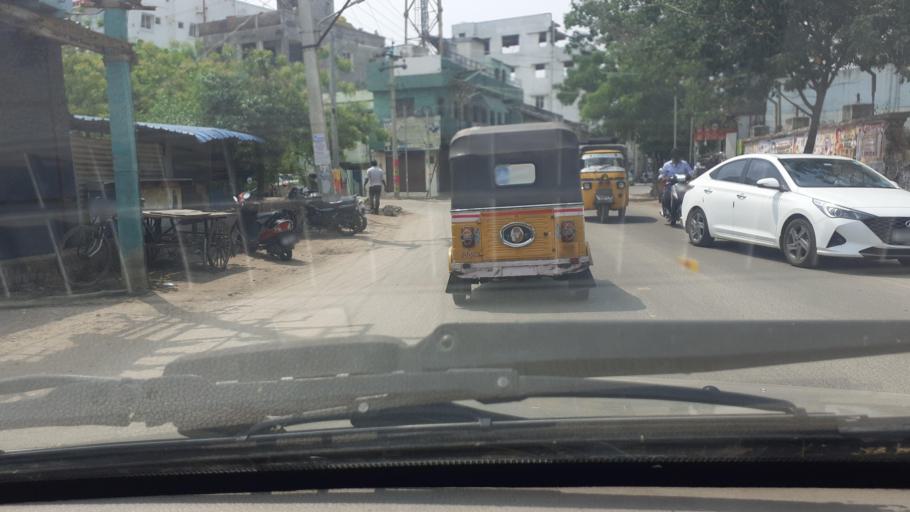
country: IN
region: Tamil Nadu
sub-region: Thoothukkudi
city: Korampallam
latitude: 8.8042
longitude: 78.1400
